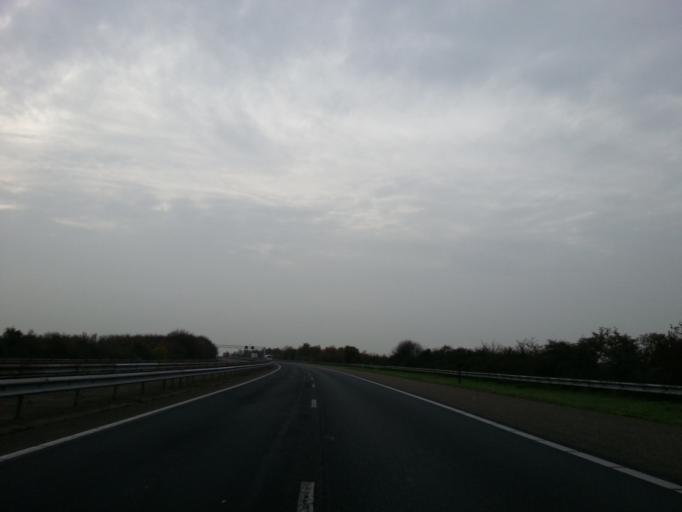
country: NL
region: North Brabant
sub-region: Gemeente Moerdijk
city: Willemstad
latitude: 51.7033
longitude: 4.3943
